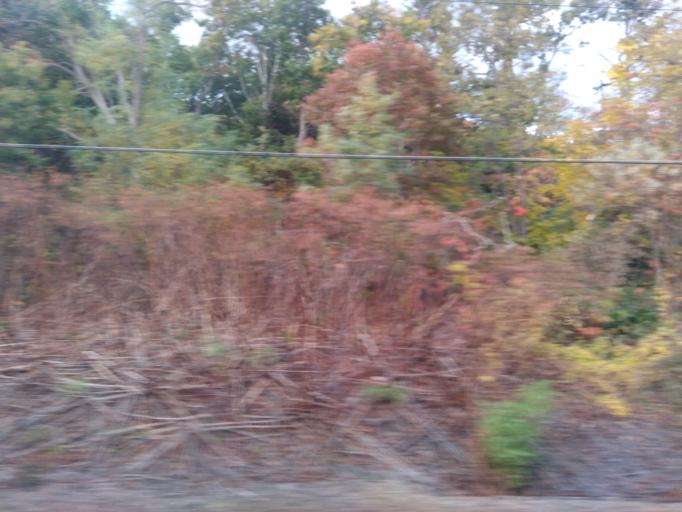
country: JP
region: Hokkaido
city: Niseko Town
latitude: 42.5890
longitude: 140.6912
